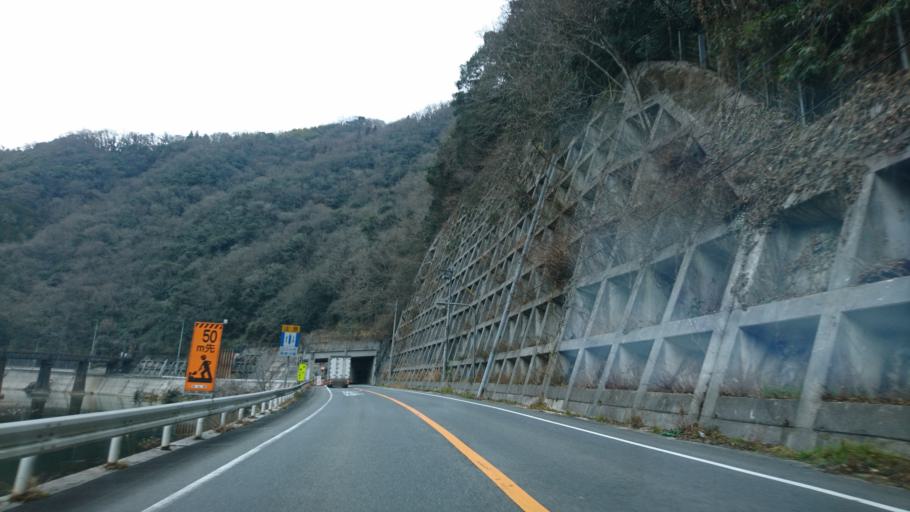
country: JP
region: Okayama
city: Niimi
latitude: 34.9122
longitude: 133.5318
